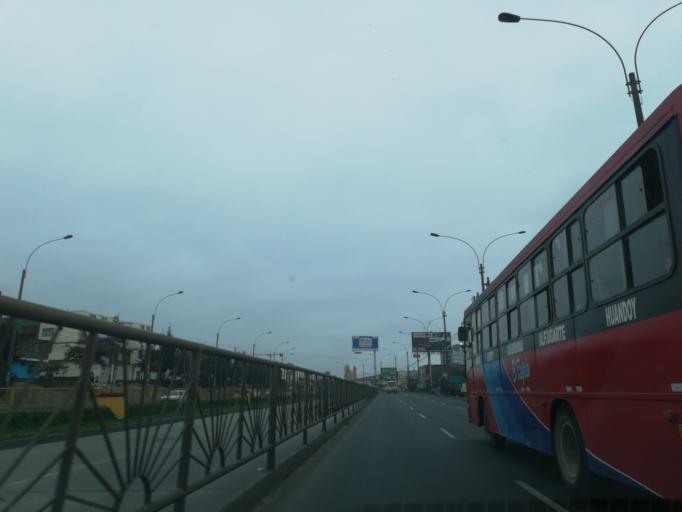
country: PE
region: Lima
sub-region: Lima
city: Independencia
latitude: -11.9907
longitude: -77.0572
